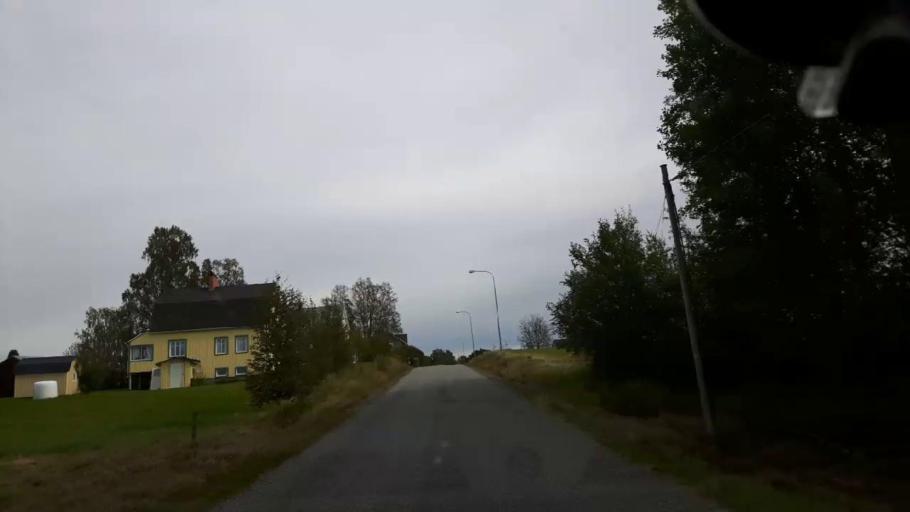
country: SE
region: Jaemtland
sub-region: Ragunda Kommun
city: Hammarstrand
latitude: 63.0086
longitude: 16.0814
